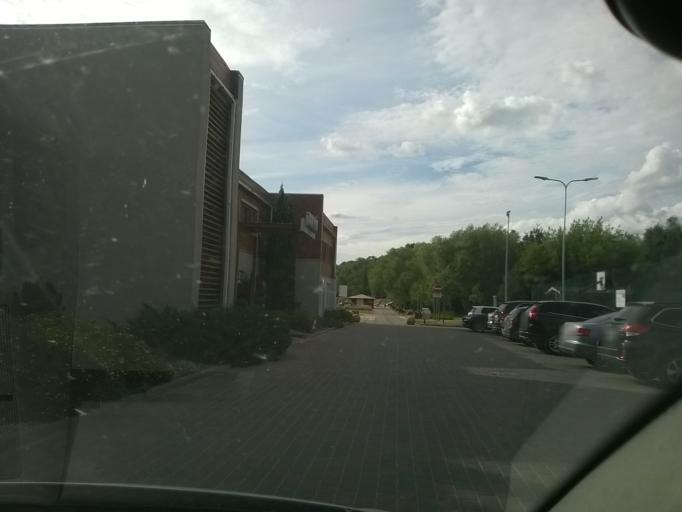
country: EE
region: Vorumaa
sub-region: Voru linn
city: Voru
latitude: 57.8432
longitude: 26.9930
